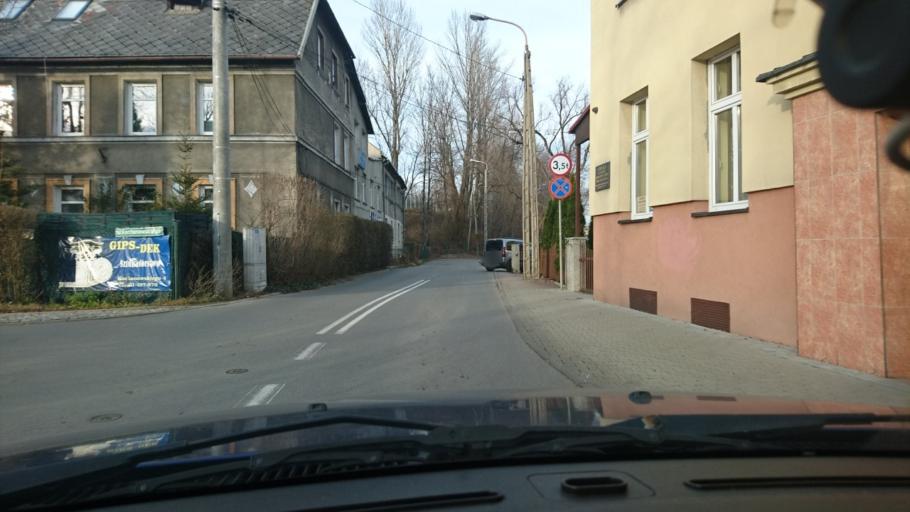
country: PL
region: Silesian Voivodeship
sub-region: Bielsko-Biala
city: Bielsko-Biala
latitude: 49.8082
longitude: 19.0419
